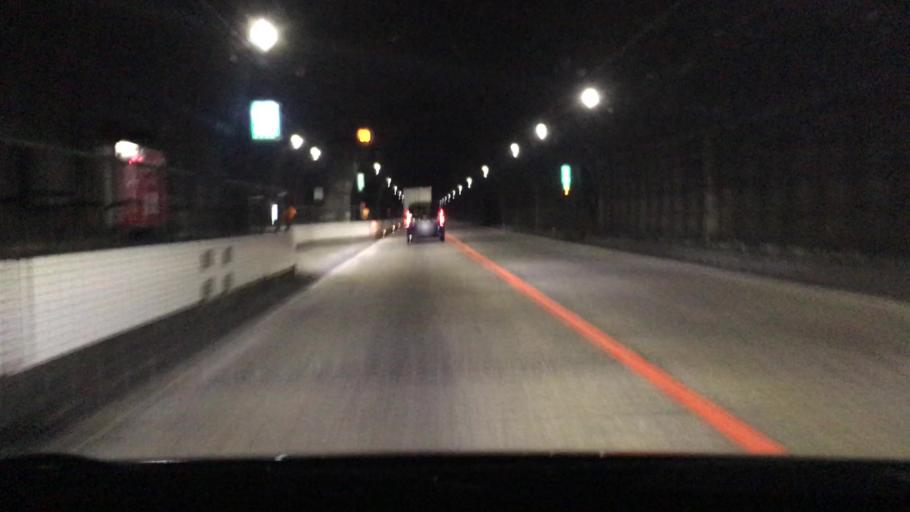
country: JP
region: Yamaguchi
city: Otake
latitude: 34.2151
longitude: 132.1927
